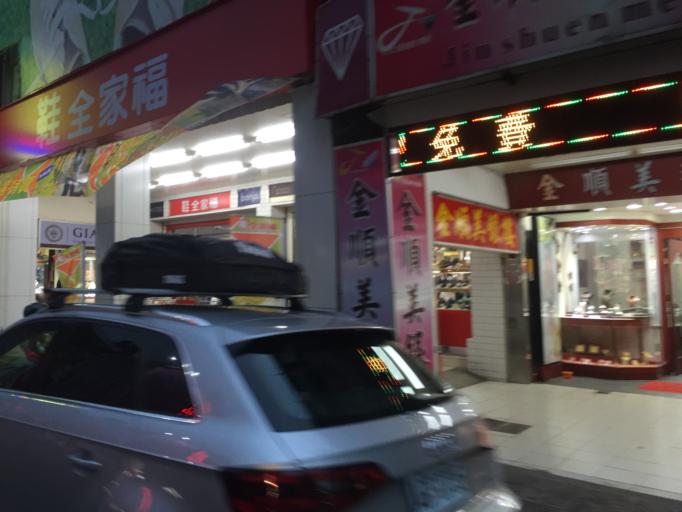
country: TW
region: Taiwan
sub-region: Yilan
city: Yilan
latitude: 24.7585
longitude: 121.7528
